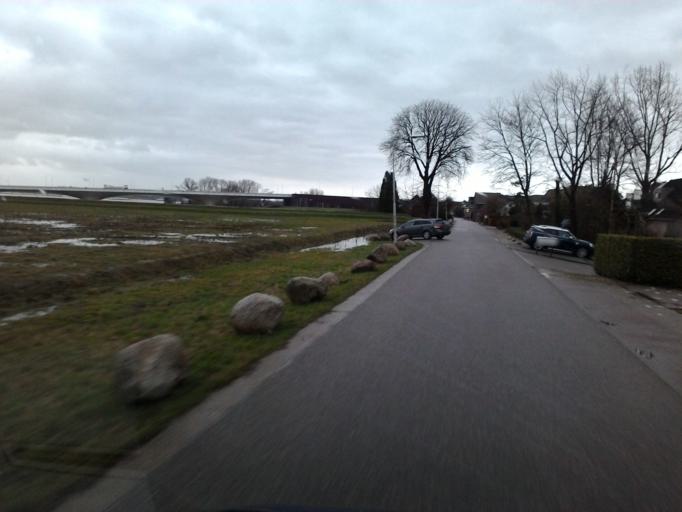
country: NL
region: Gelderland
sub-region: Gemeente Nijmegen
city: Nijmegen
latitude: 51.8543
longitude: 5.8631
